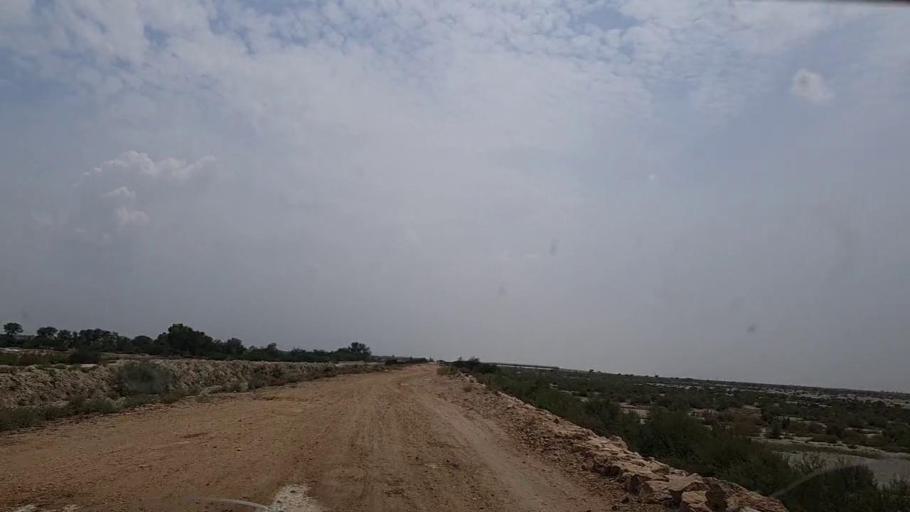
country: PK
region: Sindh
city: Phulji
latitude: 26.8282
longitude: 67.6160
